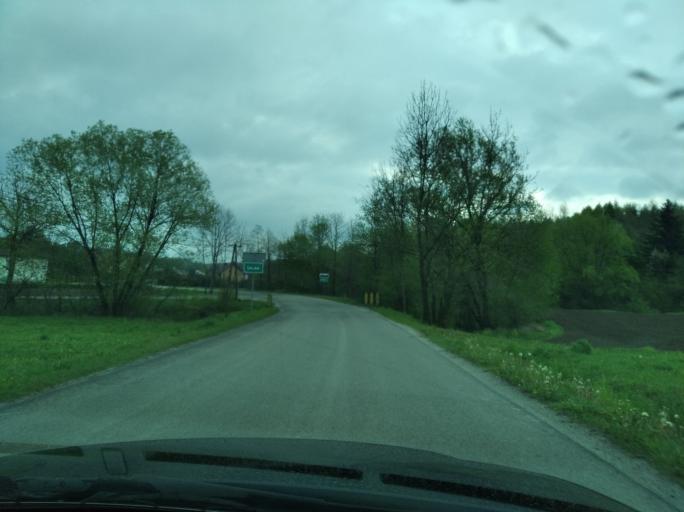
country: PL
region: Subcarpathian Voivodeship
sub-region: Powiat rzeszowski
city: Lecka
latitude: 49.8710
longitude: 22.0263
